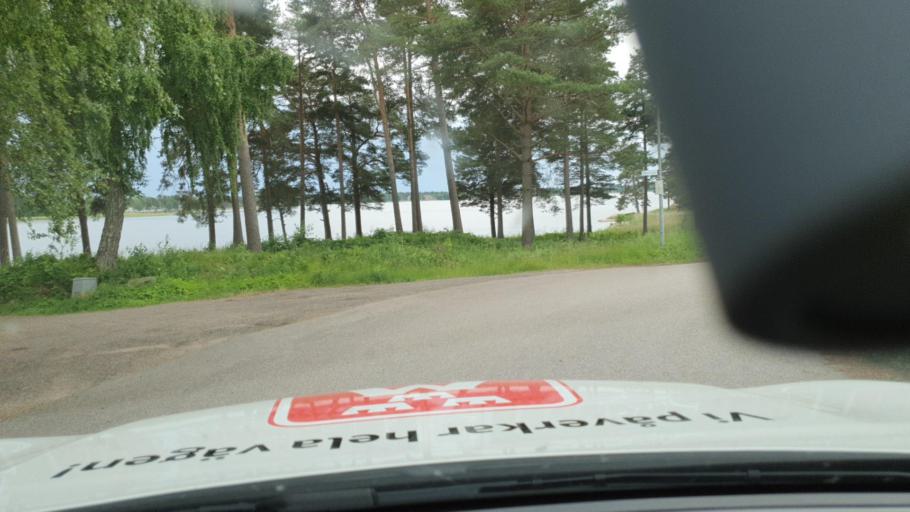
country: SE
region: Vaestra Goetaland
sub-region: Karlsborgs Kommun
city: Karlsborg
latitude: 58.5420
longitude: 14.4904
